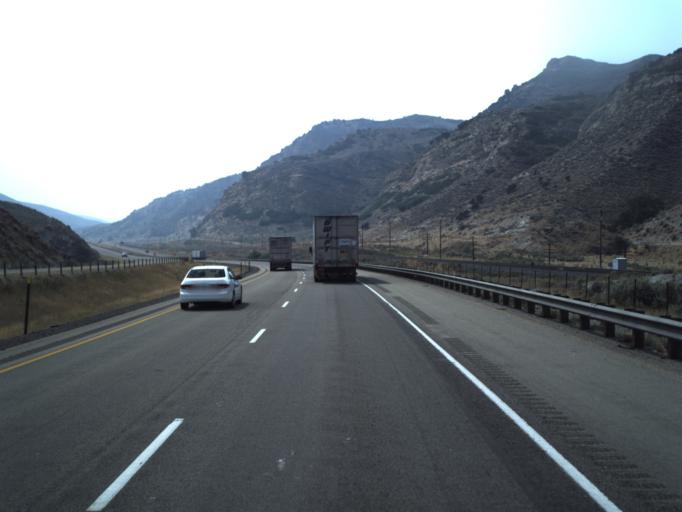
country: US
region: Utah
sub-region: Summit County
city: Coalville
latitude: 41.0652
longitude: -111.2792
